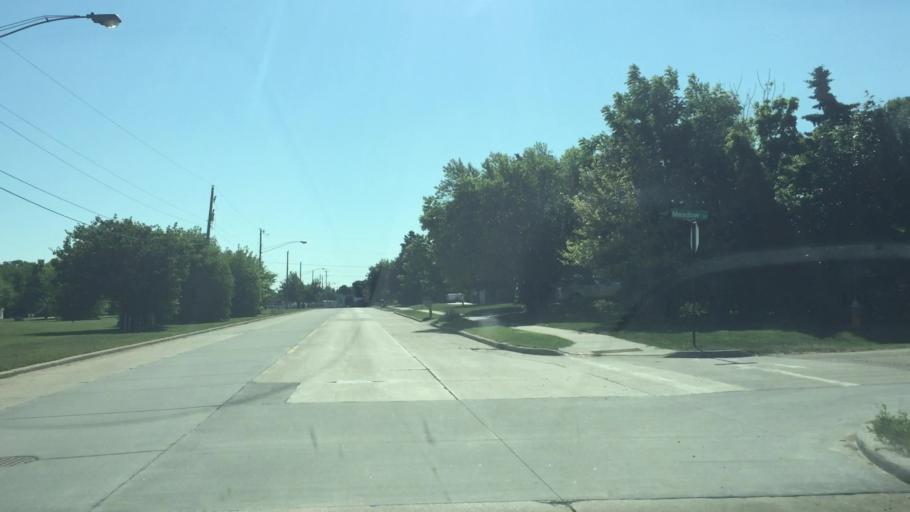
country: US
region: Wisconsin
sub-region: Winnebago County
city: Menasha
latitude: 44.2226
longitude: -88.4326
